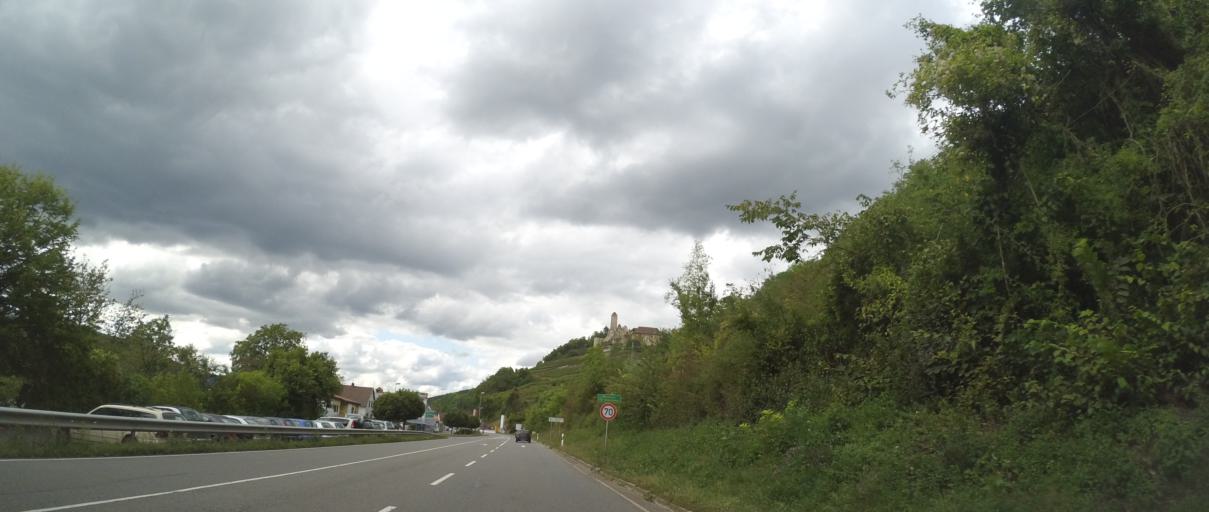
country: DE
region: Baden-Wuerttemberg
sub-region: Karlsruhe Region
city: Hassmersheim
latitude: 49.3093
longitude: 9.1494
